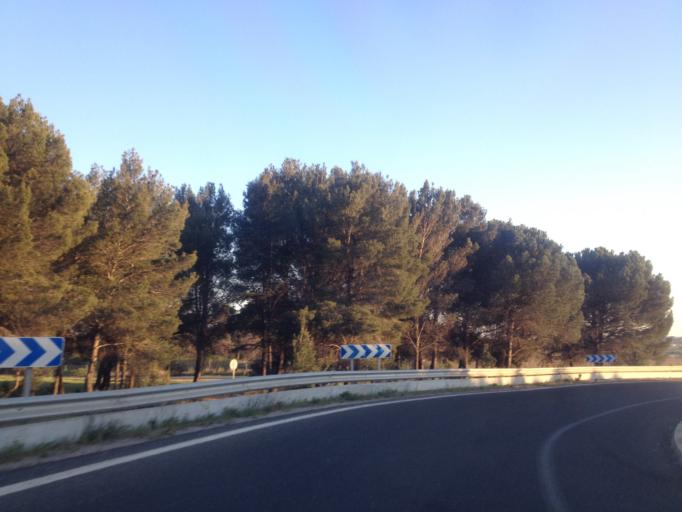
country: FR
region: Languedoc-Roussillon
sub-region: Departement de l'Herault
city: Le Cres
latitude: 43.6059
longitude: 3.9342
